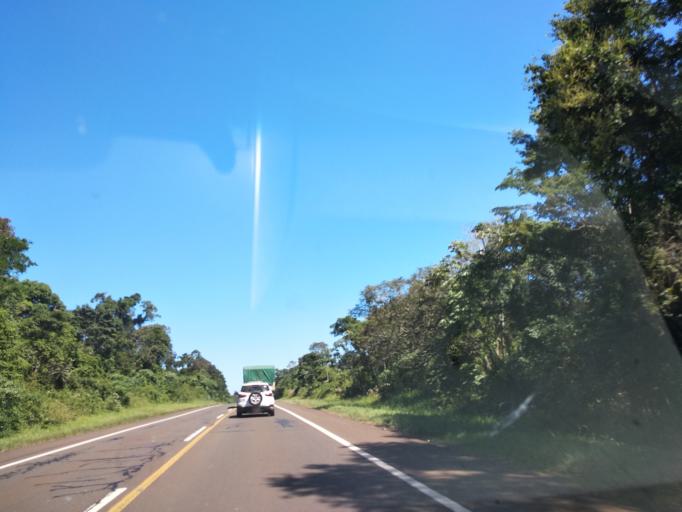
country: AR
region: Misiones
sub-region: Departamento de Iguazu
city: Puerto Iguazu
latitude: -25.7129
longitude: -54.5186
